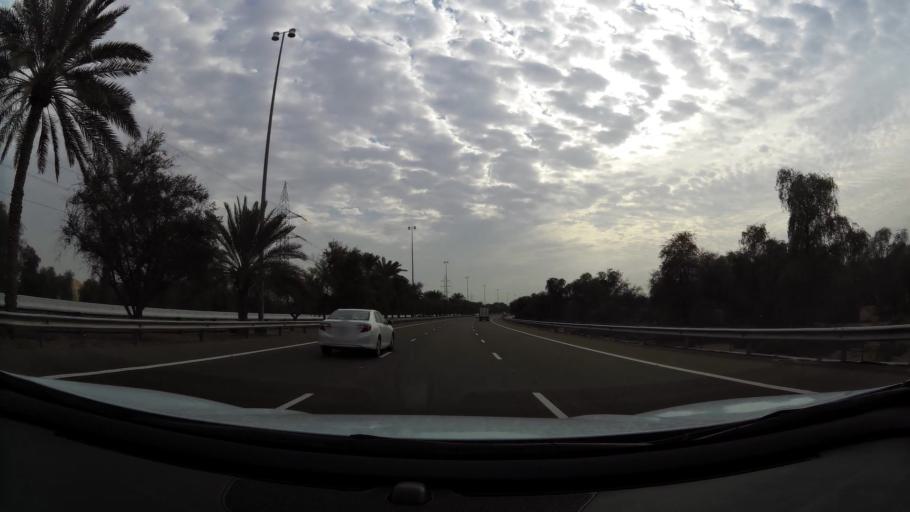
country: AE
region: Abu Dhabi
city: Al Ain
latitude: 24.1720
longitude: 55.2335
